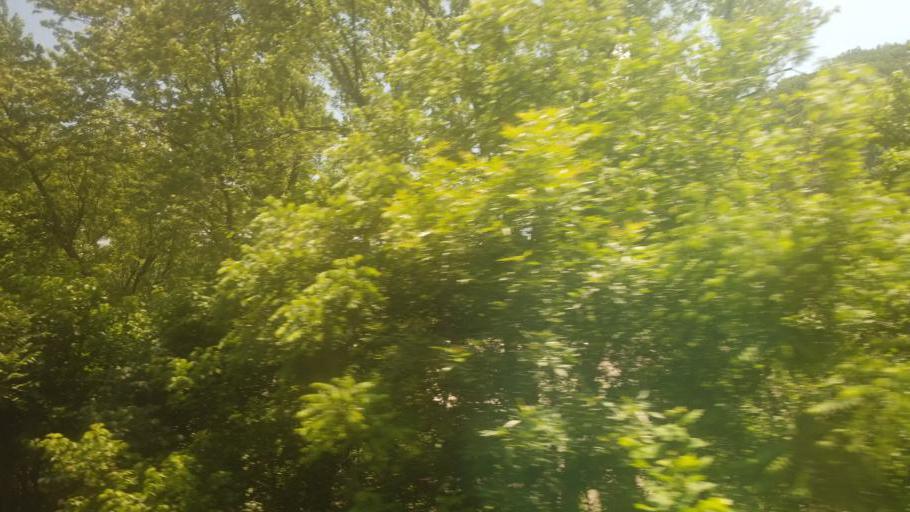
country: US
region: West Virginia
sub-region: Jefferson County
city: Bolivar
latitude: 39.3247
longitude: -77.7211
